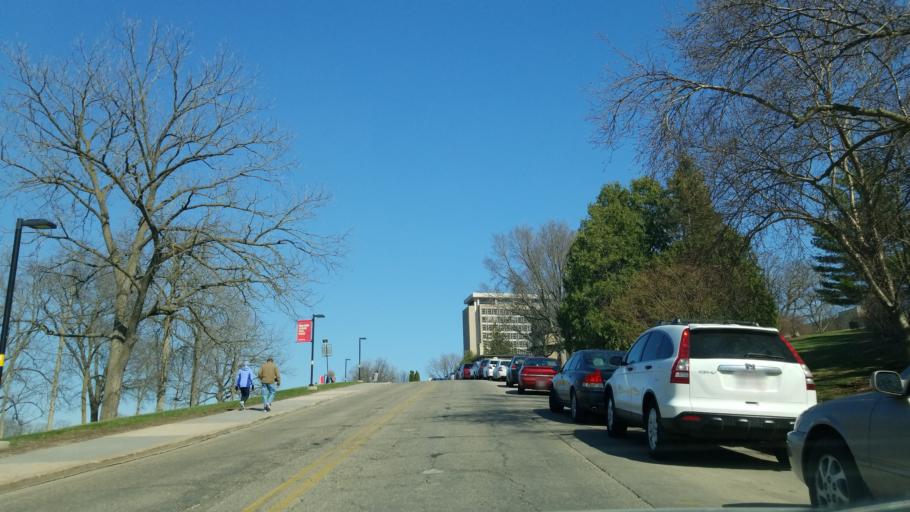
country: US
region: Wisconsin
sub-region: Dane County
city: Madison
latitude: 43.0766
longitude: -89.4106
